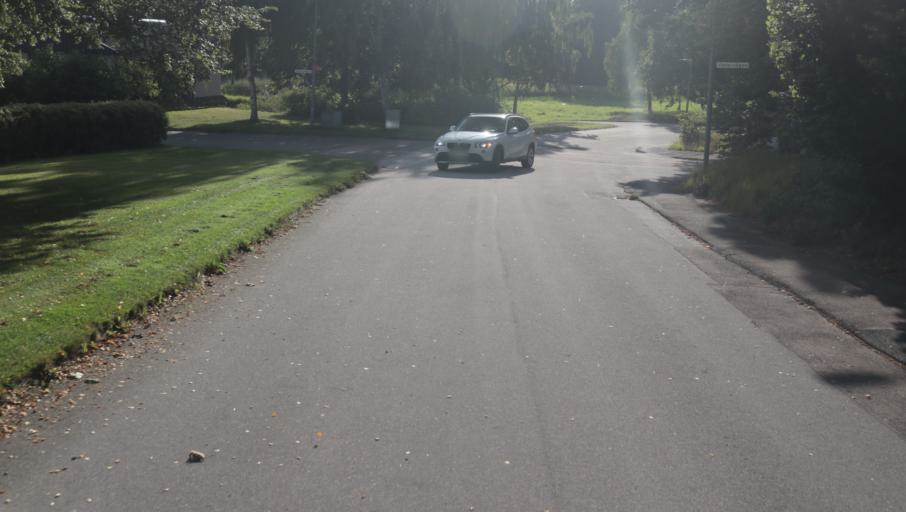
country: SE
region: Blekinge
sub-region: Karlshamns Kommun
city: Karlshamn
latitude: 56.1632
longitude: 14.8911
